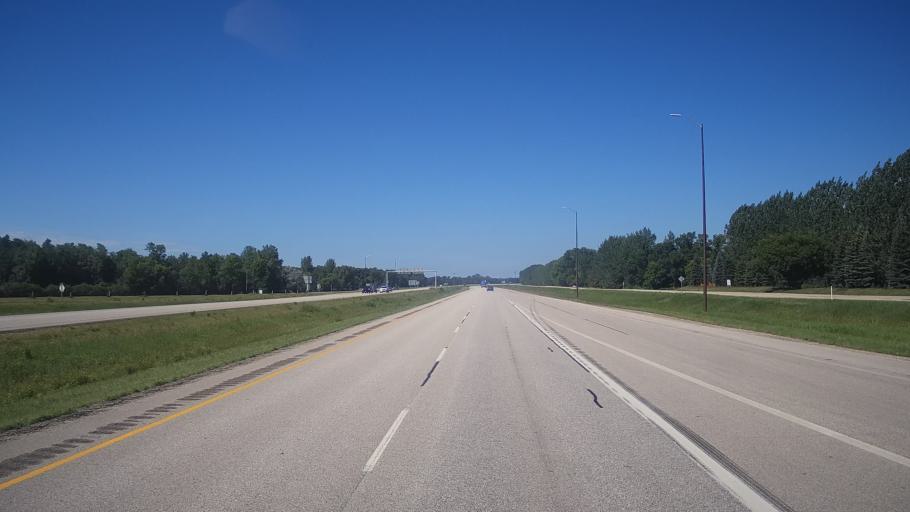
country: CA
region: Manitoba
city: Portage la Prairie
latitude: 49.9529
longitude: -98.2778
